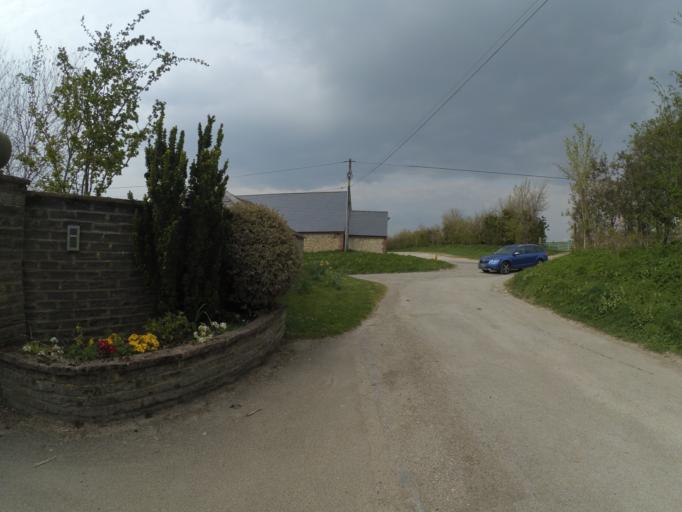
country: GB
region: England
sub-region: West Sussex
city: Arundel
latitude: 50.8738
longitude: -0.5273
